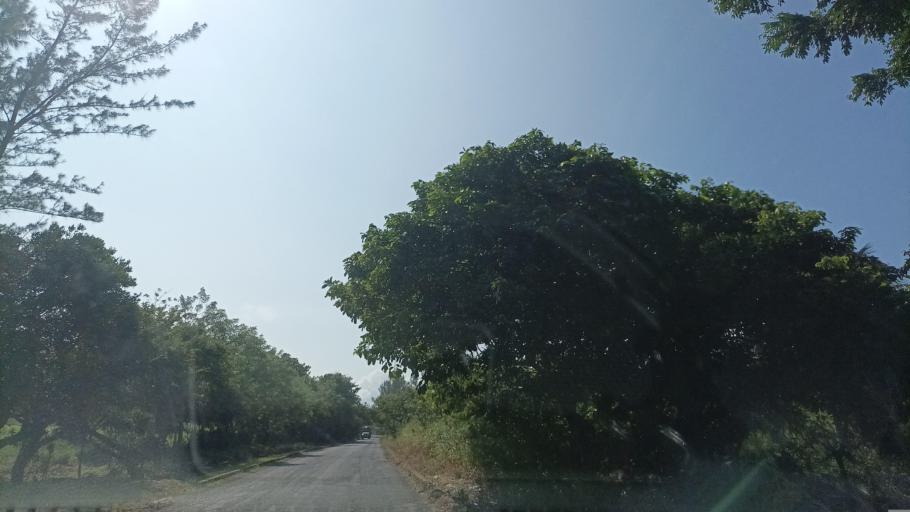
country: MX
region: Veracruz
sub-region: Pajapan
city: Pajapan
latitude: 18.2209
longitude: -94.6159
